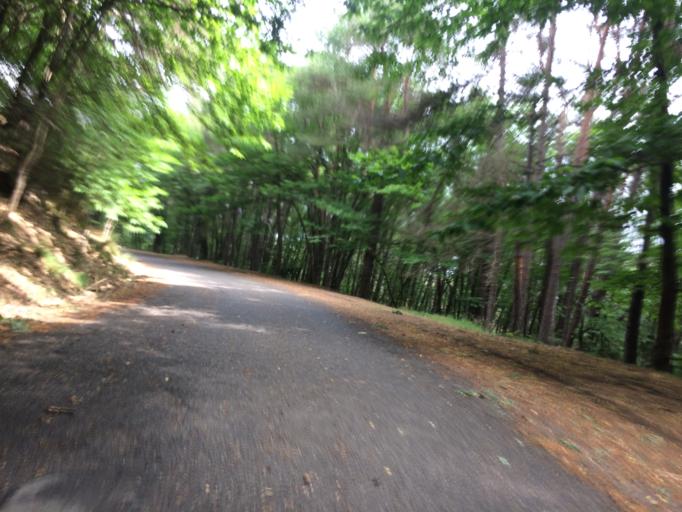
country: IT
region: Liguria
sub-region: Provincia di Imperia
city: Bajardo
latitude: 43.8818
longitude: 7.7402
